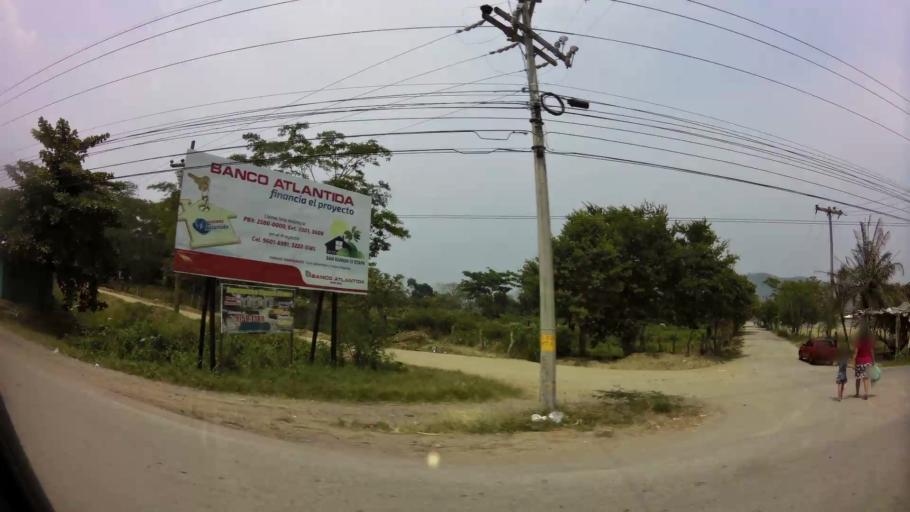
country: HN
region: Cortes
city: Villanueva
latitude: 15.3039
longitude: -87.9846
